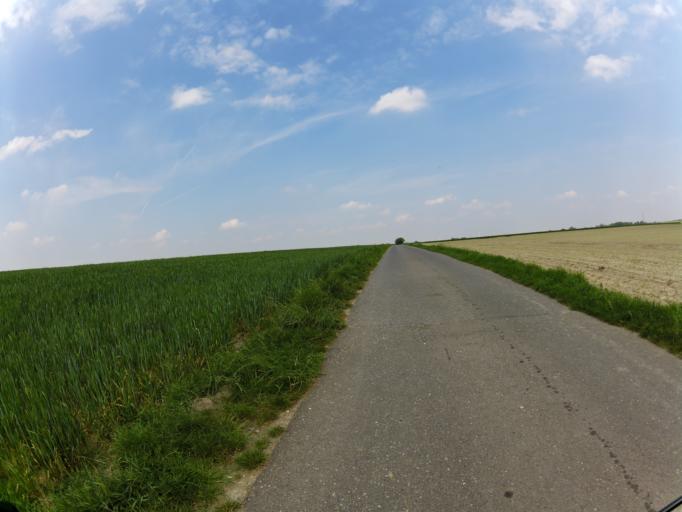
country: DE
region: North Rhine-Westphalia
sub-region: Regierungsbezirk Koln
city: Gangelt
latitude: 50.9938
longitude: 6.0234
